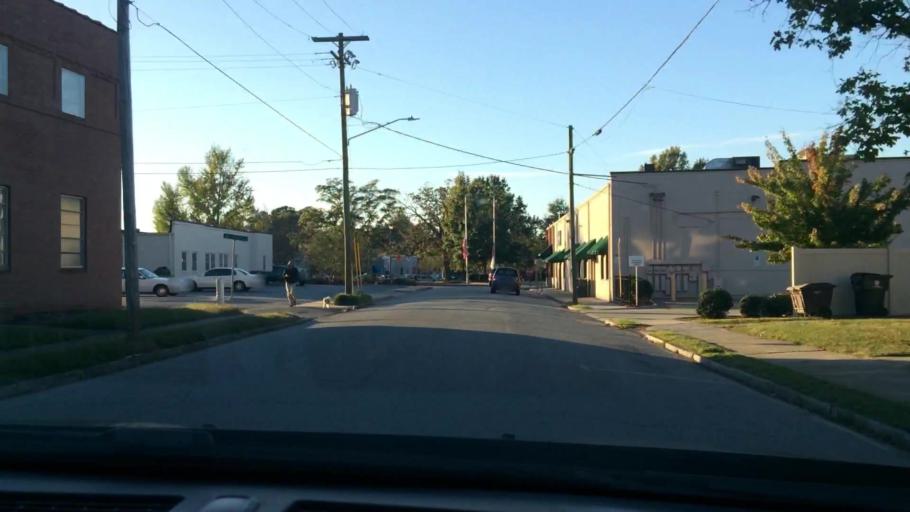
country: US
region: North Carolina
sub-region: Pitt County
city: Farmville
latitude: 35.5978
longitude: -77.5833
